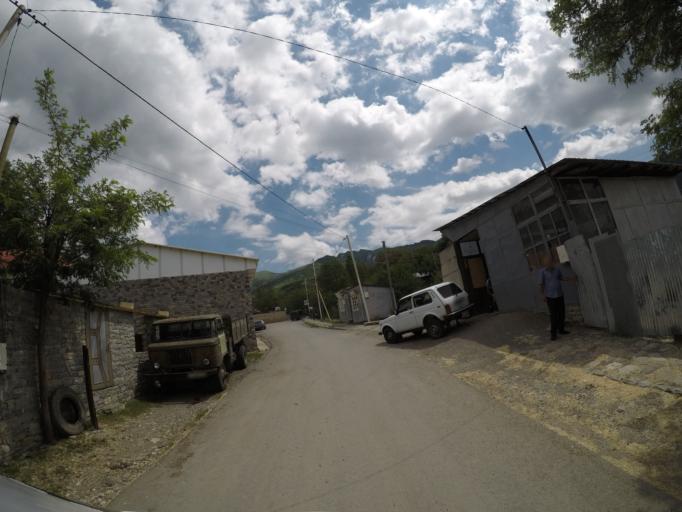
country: AZ
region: Ismayilli
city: Basqal
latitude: 40.8490
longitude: 48.3855
